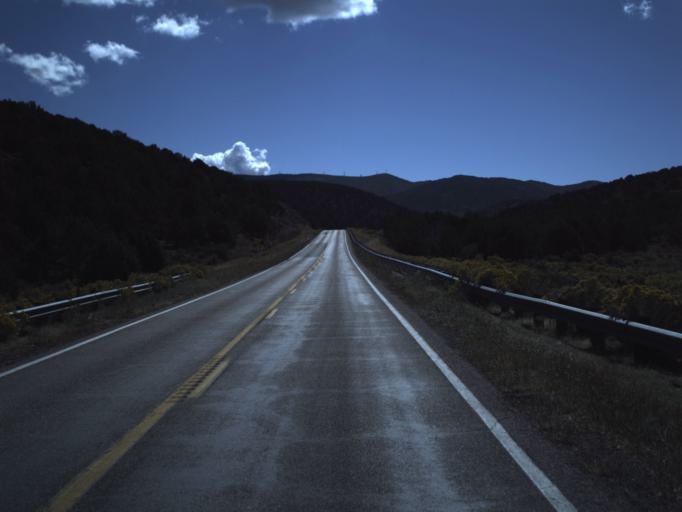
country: US
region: Utah
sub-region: Washington County
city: Enterprise
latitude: 37.5562
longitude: -113.6898
